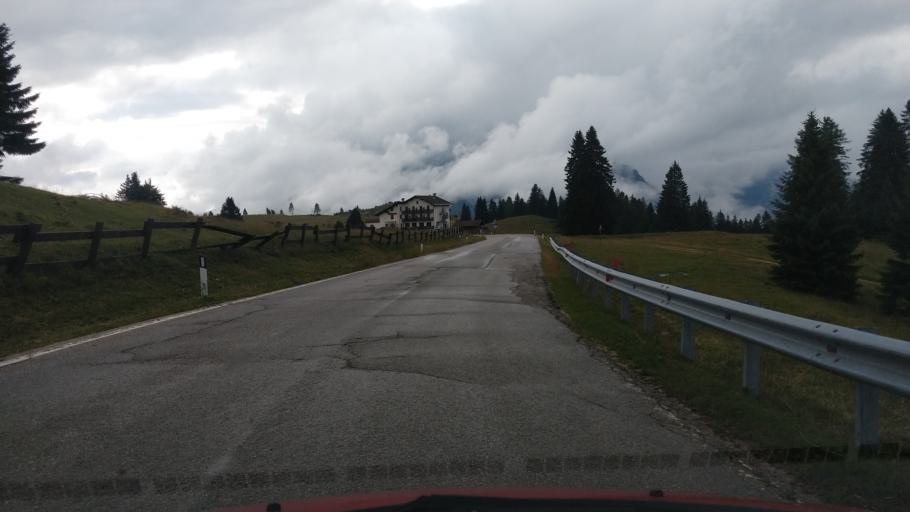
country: IT
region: Veneto
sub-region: Provincia di Vicenza
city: Lastebasse
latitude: 45.9123
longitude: 11.2365
